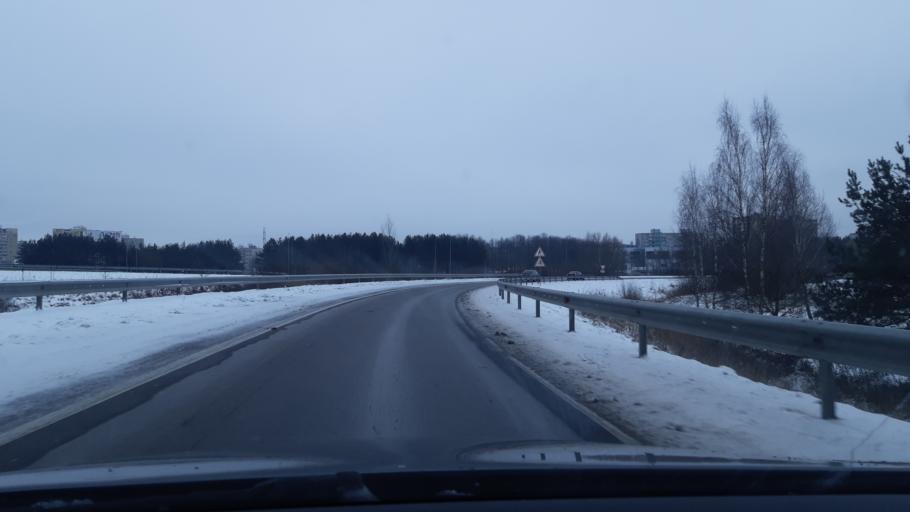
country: LT
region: Kauno apskritis
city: Dainava (Kaunas)
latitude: 54.9332
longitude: 23.9777
